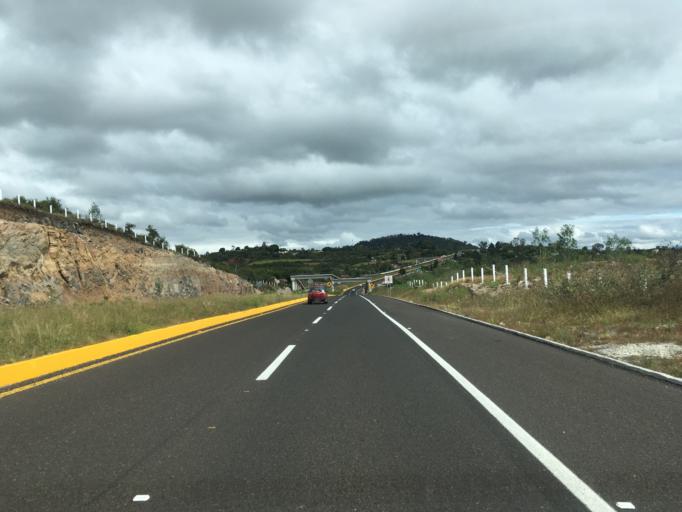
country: MX
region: Hidalgo
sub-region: Atotonilco el Grande
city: Santa Maria Amajac
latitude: 20.3897
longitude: -98.7233
